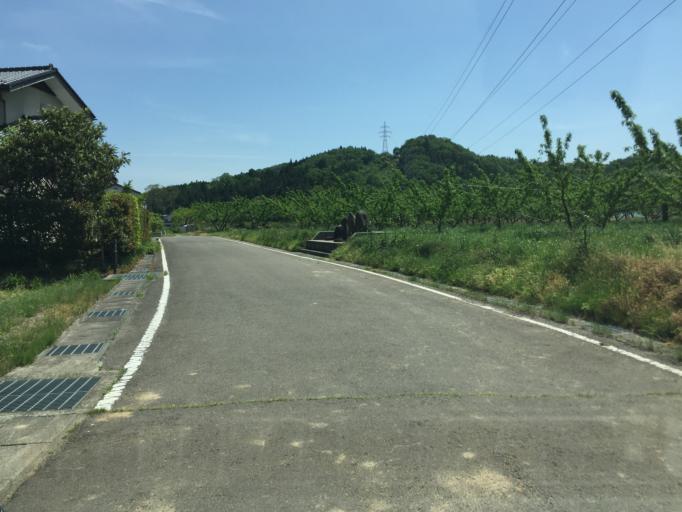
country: JP
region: Fukushima
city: Fukushima-shi
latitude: 37.7312
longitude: 140.4121
